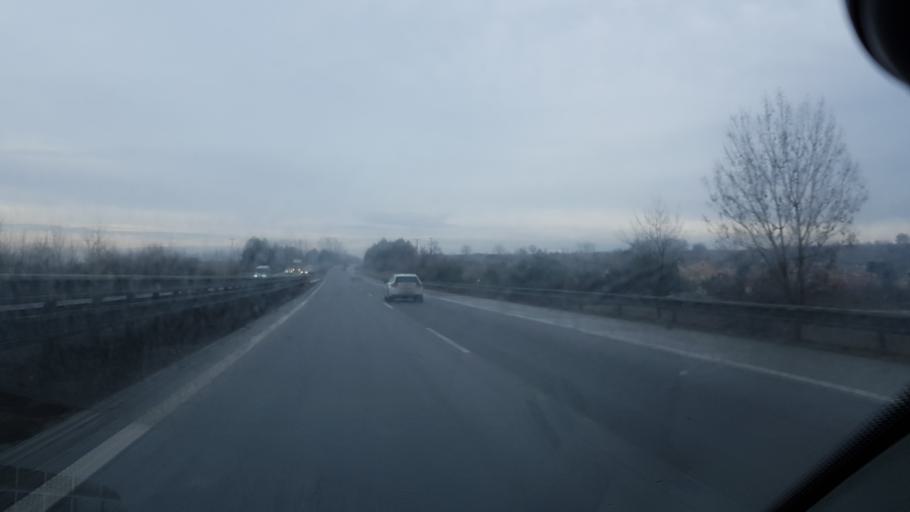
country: CZ
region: South Moravian
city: Rousinov
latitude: 49.1931
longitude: 16.8866
